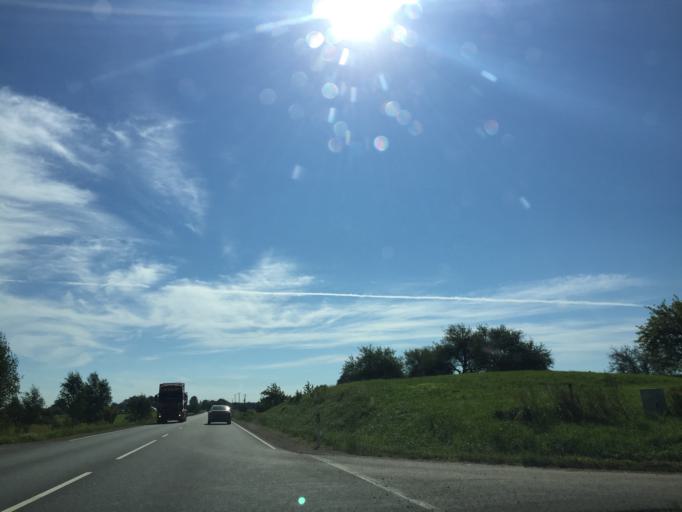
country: LV
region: Ikskile
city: Ikskile
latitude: 56.8698
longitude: 24.5445
